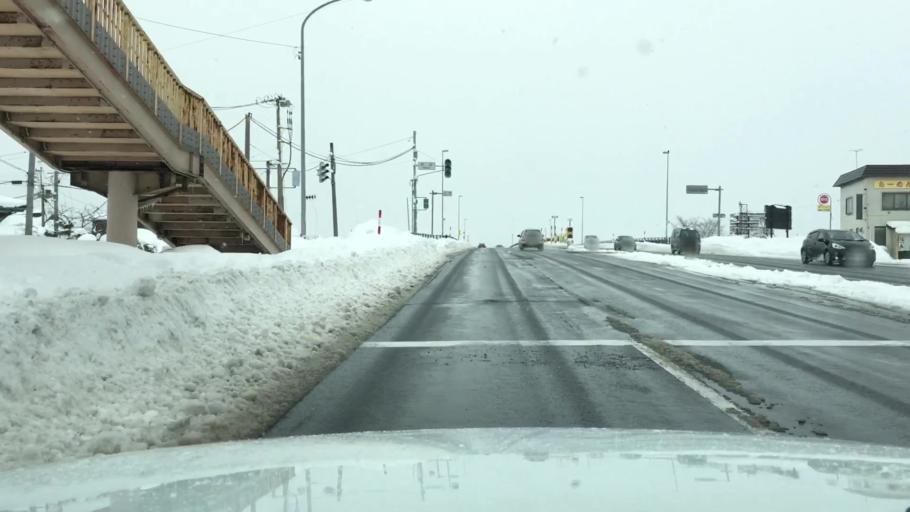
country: JP
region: Aomori
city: Hirosaki
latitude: 40.6437
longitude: 140.4940
